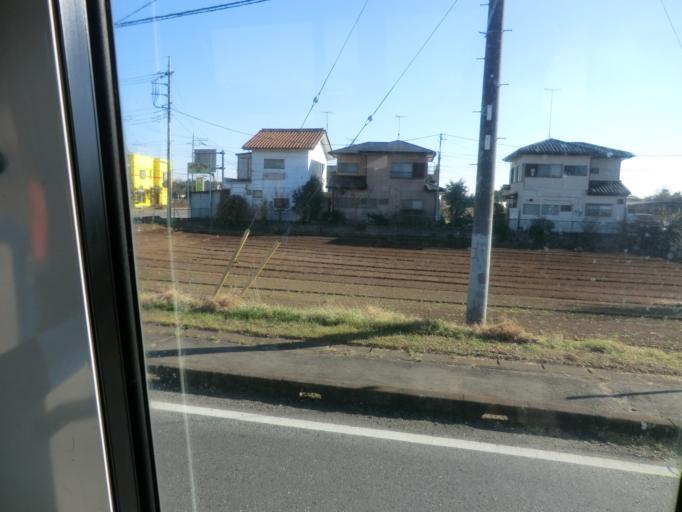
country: JP
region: Ibaraki
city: Ushiku
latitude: 36.0224
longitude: 140.0777
